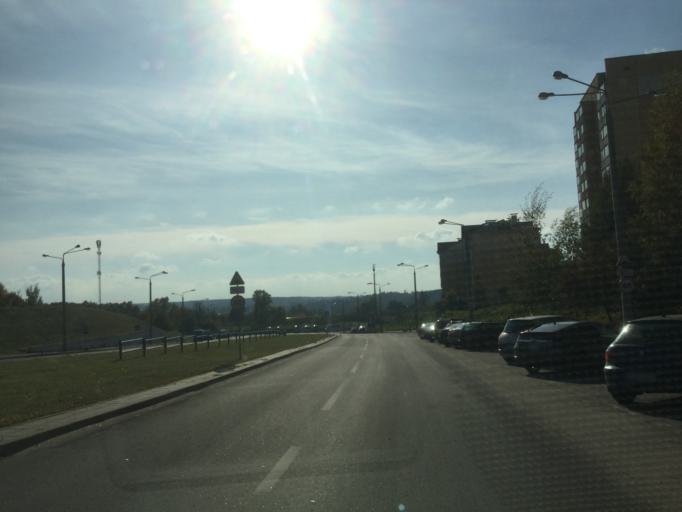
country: BY
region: Vitebsk
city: Vitebsk
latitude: 55.1562
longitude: 30.2121
